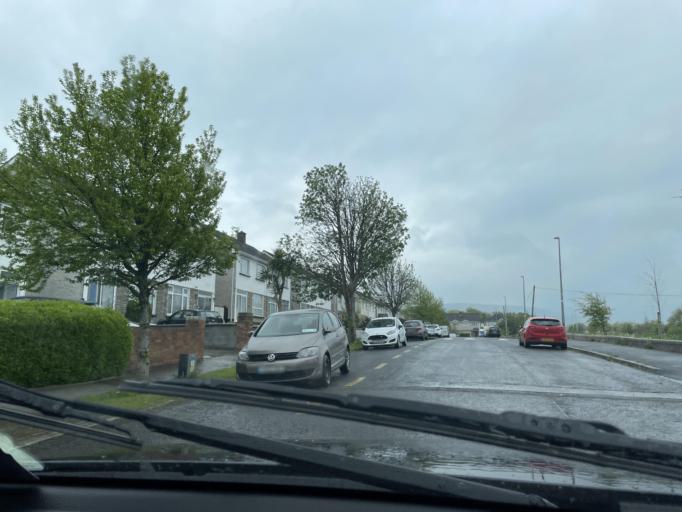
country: IE
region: Leinster
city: Dundrum
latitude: 53.2894
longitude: -6.2651
